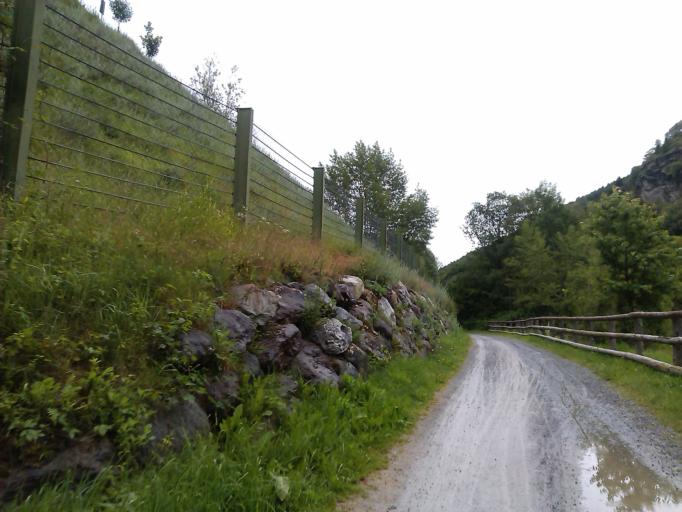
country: IT
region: Trentino-Alto Adige
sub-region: Bolzano
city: Lasa
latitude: 46.6136
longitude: 10.7331
